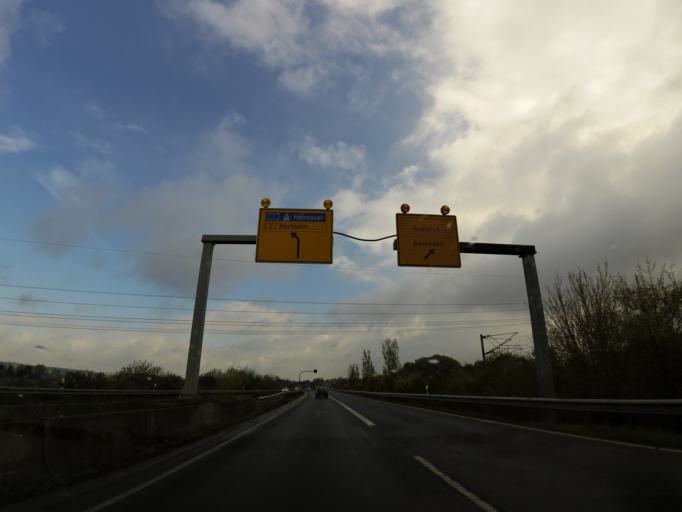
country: DE
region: Lower Saxony
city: Bovenden
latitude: 51.5789
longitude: 9.9230
